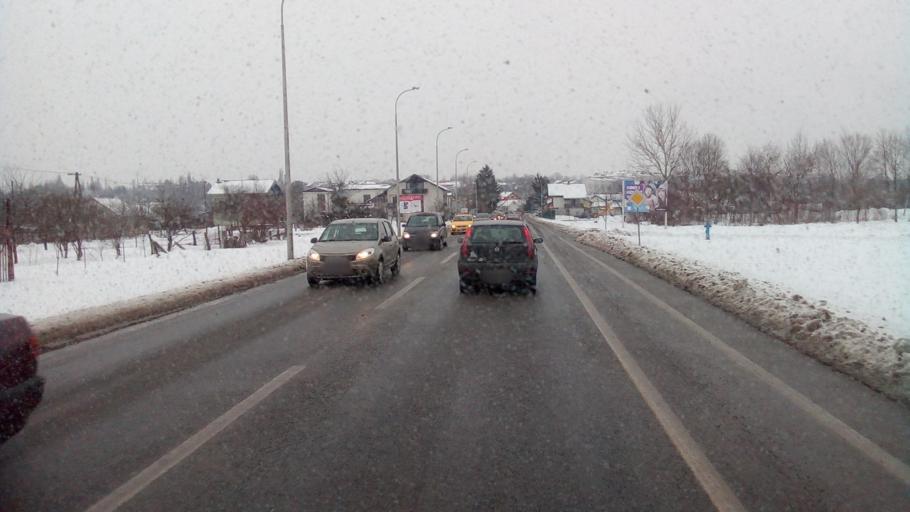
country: HR
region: Sisacko-Moslavacka
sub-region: Grad Sisak
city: Sisak
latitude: 45.4599
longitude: 16.3718
